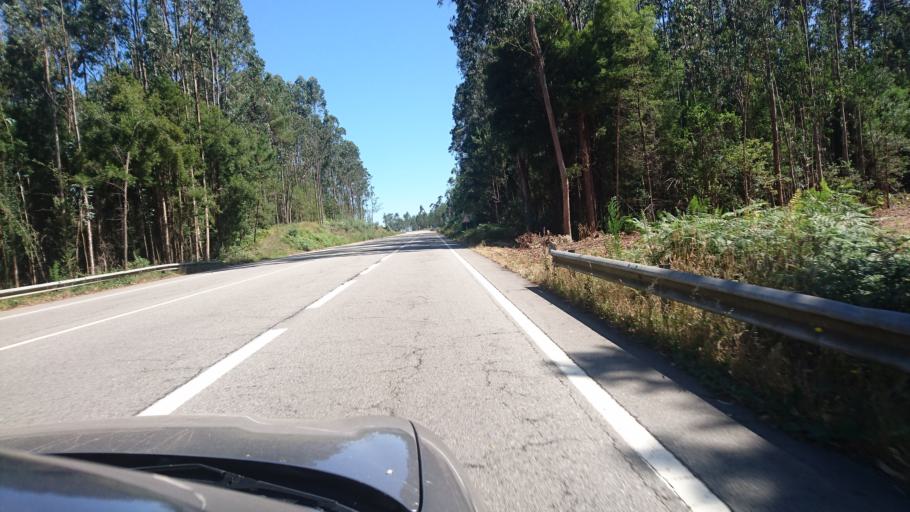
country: PT
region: Aveiro
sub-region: Santa Maria da Feira
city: Rio Meao
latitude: 40.9343
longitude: -8.5831
